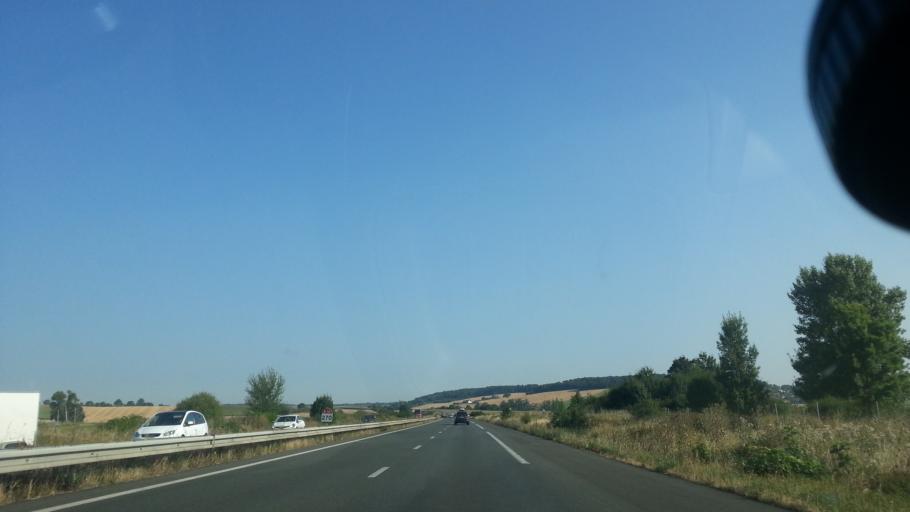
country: FR
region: Poitou-Charentes
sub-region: Departement de la Vienne
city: Antran
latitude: 46.8574
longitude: 0.5258
